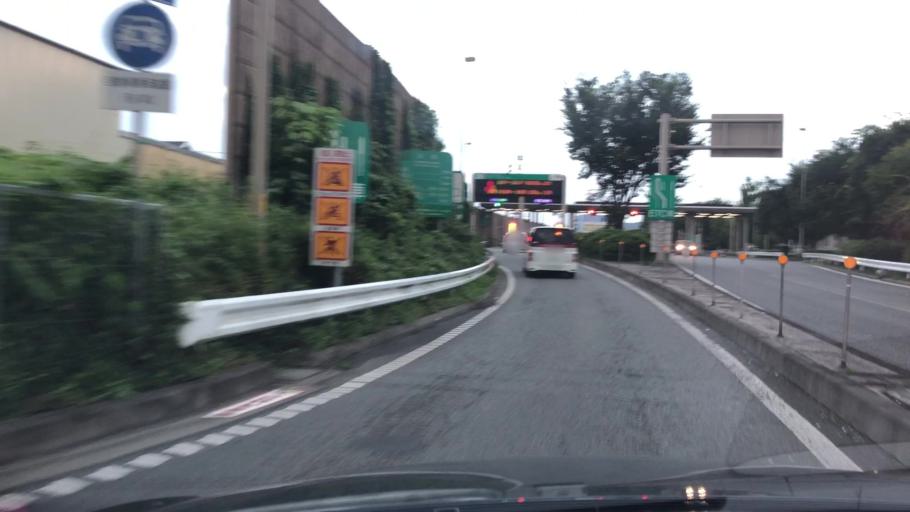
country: JP
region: Tokyo
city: Fussa
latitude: 35.7392
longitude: 139.2840
